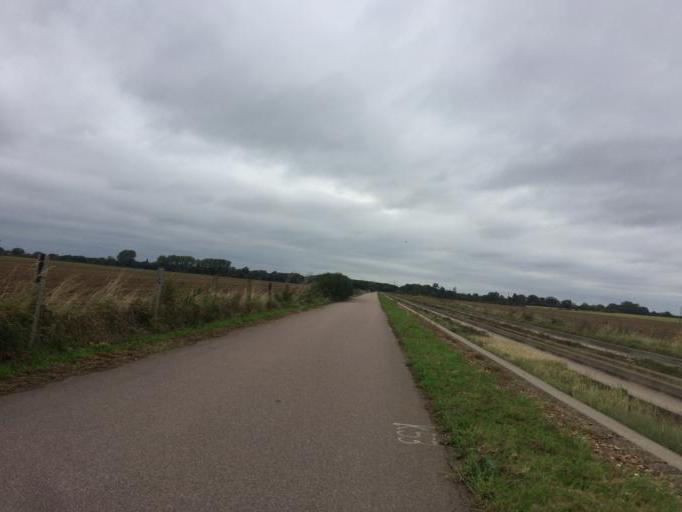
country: GB
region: England
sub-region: Cambridgeshire
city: Histon
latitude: 52.2554
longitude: 0.0896
